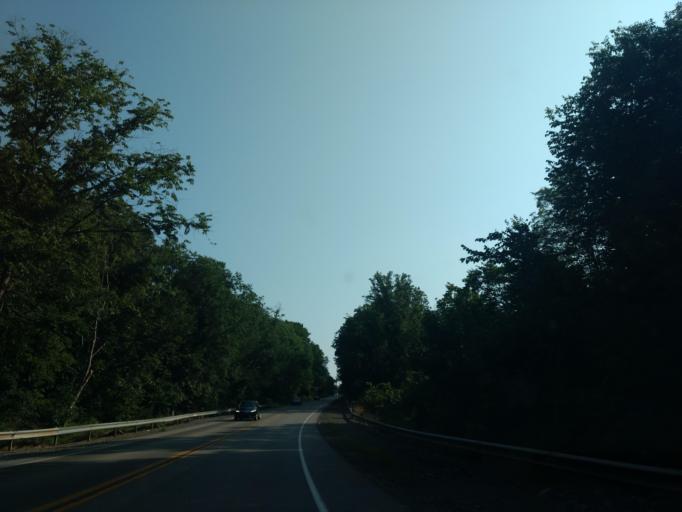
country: US
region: Pennsylvania
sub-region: Butler County
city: Zelienople
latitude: 40.8870
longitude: -80.1378
